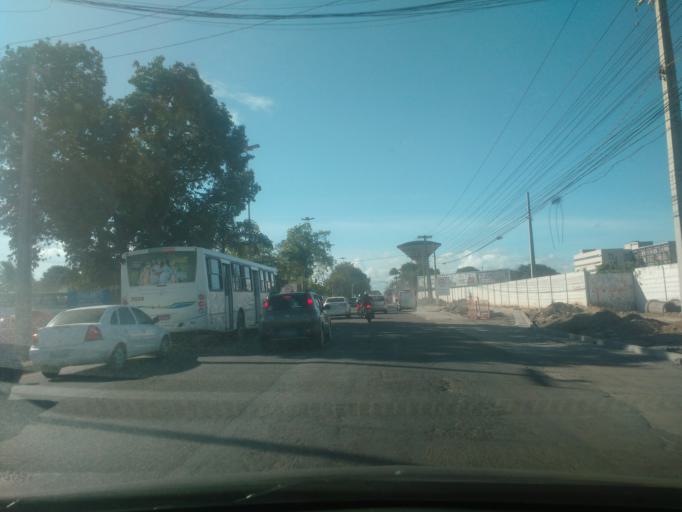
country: BR
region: Alagoas
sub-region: Satuba
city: Satuba
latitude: -9.5621
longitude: -35.7791
